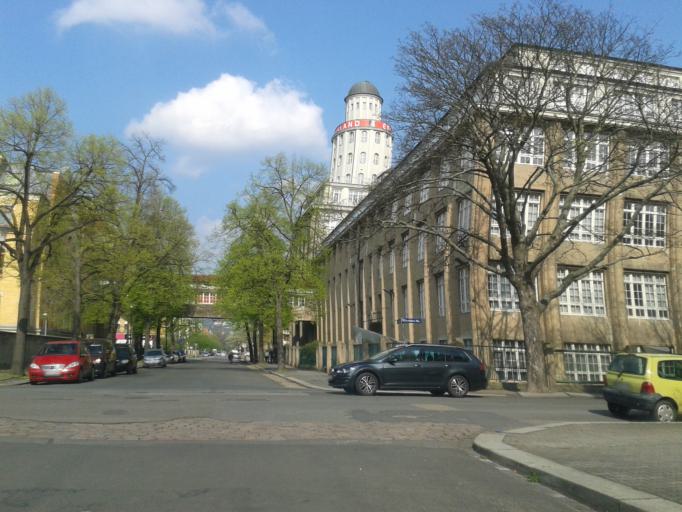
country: DE
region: Saxony
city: Albertstadt
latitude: 51.0414
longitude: 13.7968
